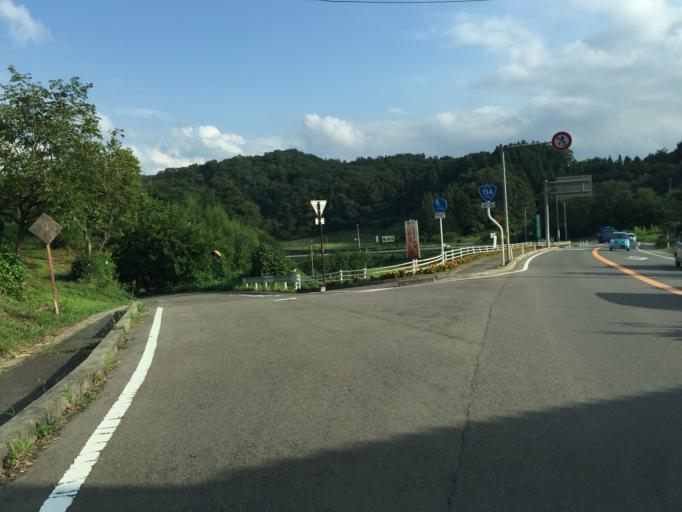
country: JP
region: Fukushima
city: Fukushima-shi
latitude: 37.6845
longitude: 140.5490
